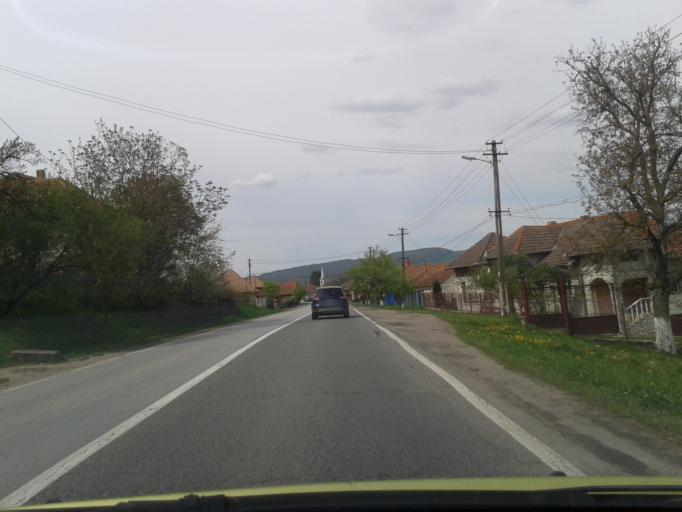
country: RO
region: Hunedoara
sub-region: Comuna Dobra
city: Dobra
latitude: 45.9094
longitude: 22.5760
